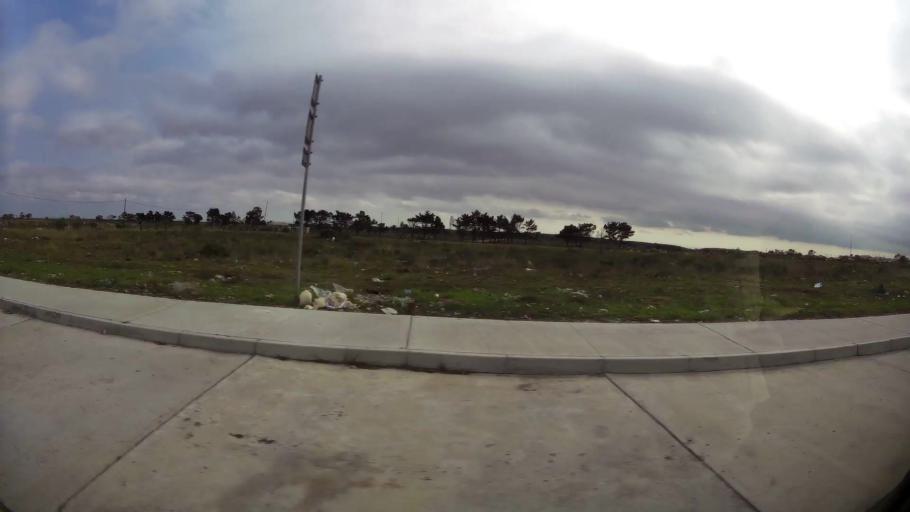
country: ZA
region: Eastern Cape
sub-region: Nelson Mandela Bay Metropolitan Municipality
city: Port Elizabeth
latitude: -33.9183
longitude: 25.5299
